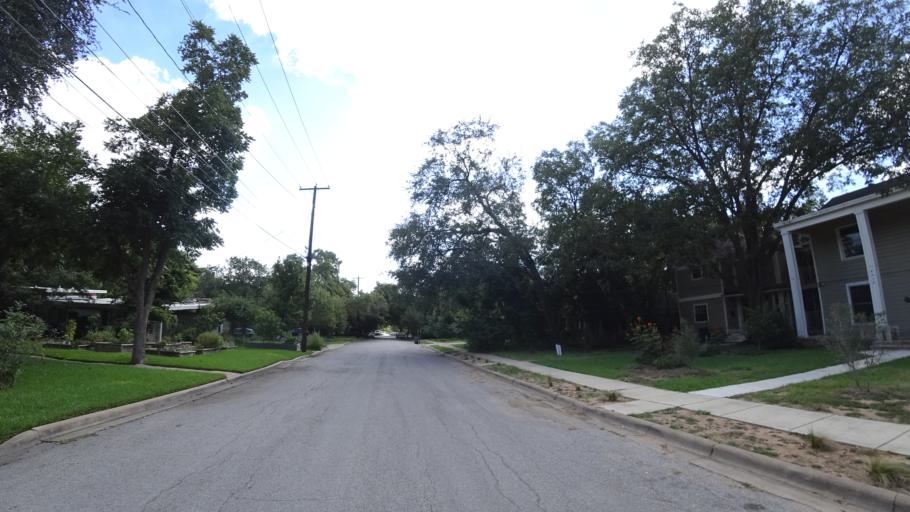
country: US
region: Texas
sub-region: Travis County
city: Austin
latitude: 30.3079
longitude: -97.7193
